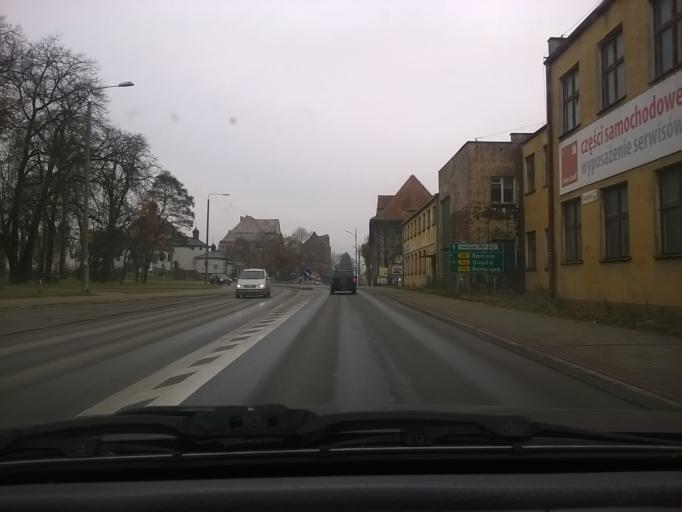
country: PL
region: Warmian-Masurian Voivodeship
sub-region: Powiat ketrzynski
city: Ketrzyn
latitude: 54.0738
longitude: 21.3769
